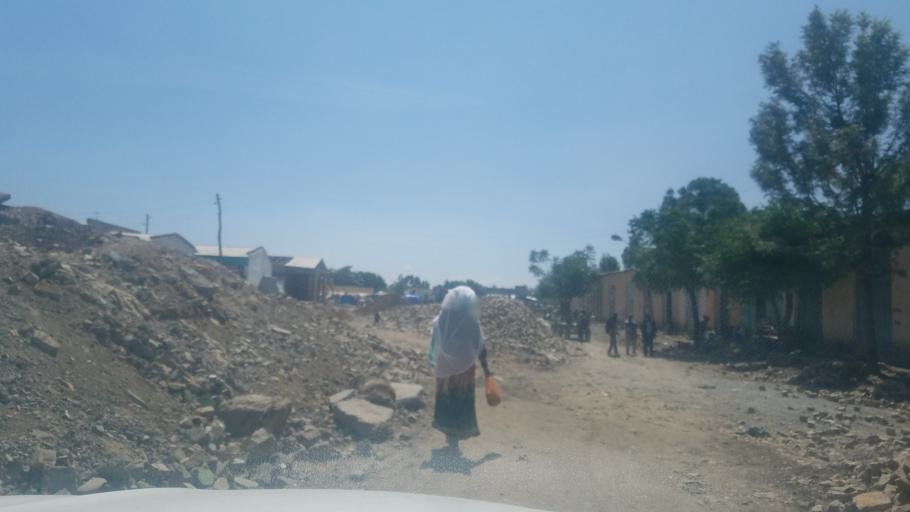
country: ET
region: Tigray
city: Mekele
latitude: 13.7954
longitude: 39.5988
